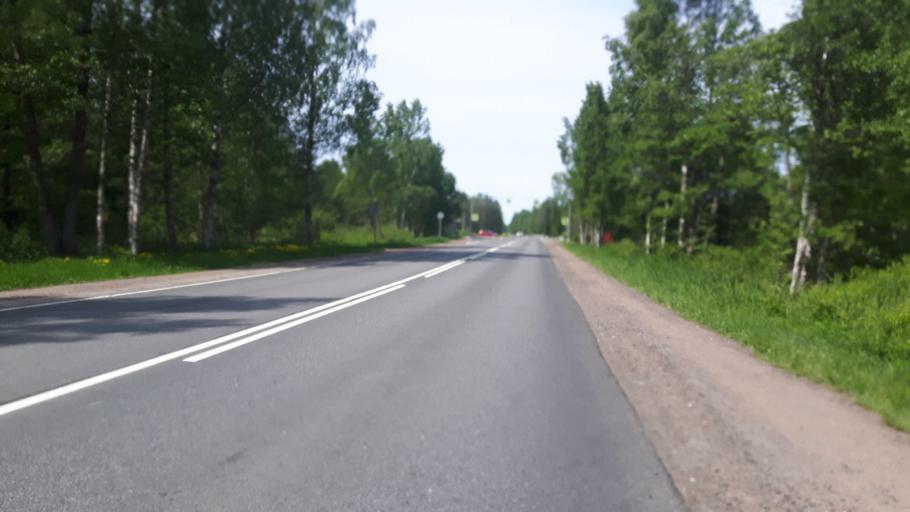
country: RU
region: Leningrad
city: Ust'-Luga
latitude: 59.6508
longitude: 28.3613
